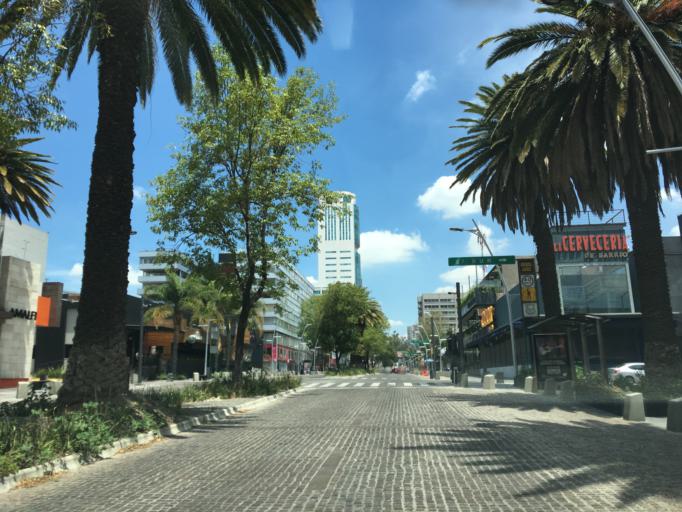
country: MX
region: Puebla
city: Puebla
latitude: 19.0521
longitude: -98.2191
